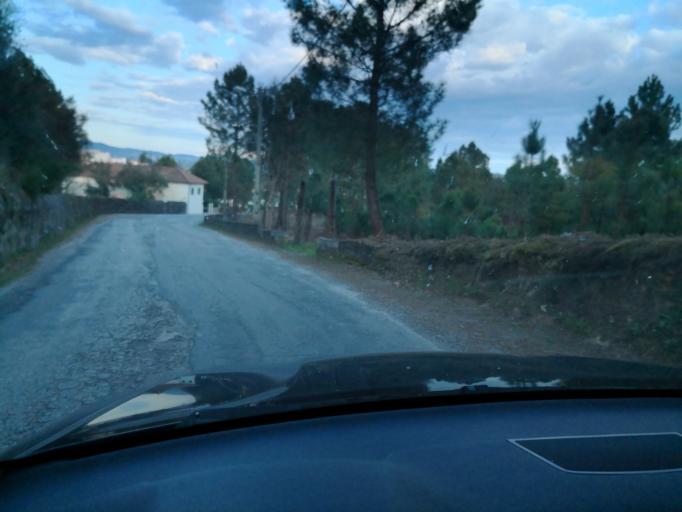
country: PT
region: Vila Real
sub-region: Vila Real
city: Vila Real
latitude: 41.2980
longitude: -7.7692
